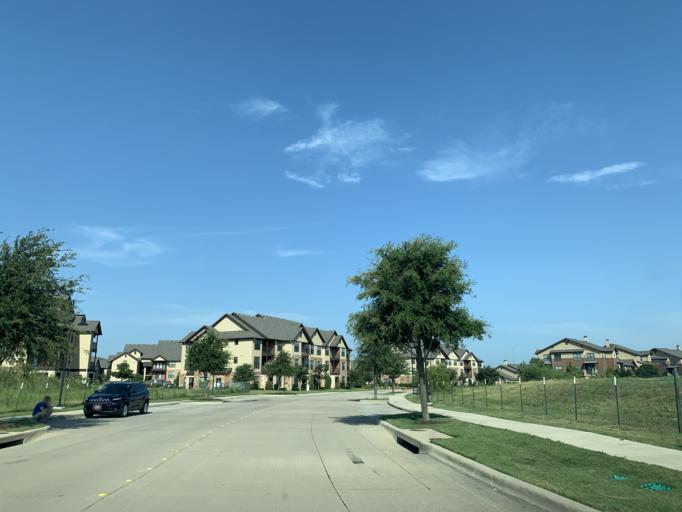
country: US
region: Texas
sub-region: Tarrant County
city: Blue Mound
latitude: 32.8922
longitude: -97.3100
